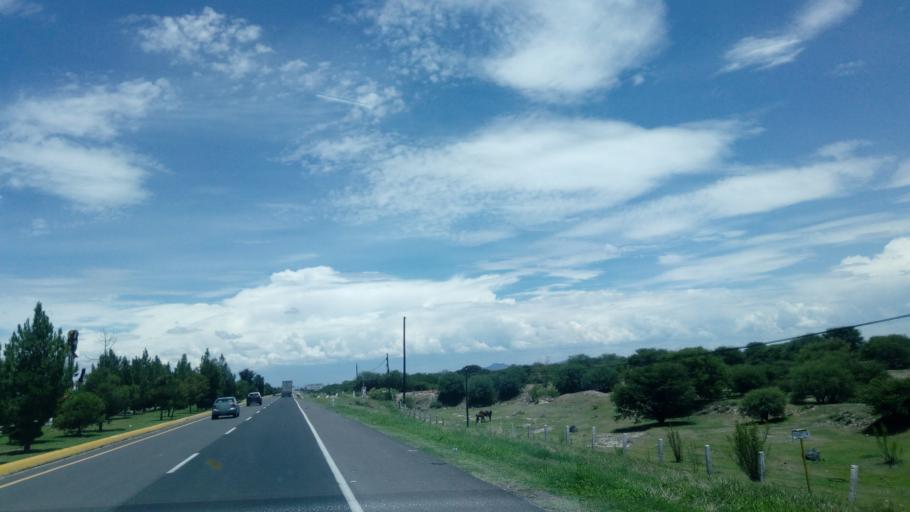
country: MX
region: Durango
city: Victoria de Durango
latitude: 24.1041
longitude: -104.5621
